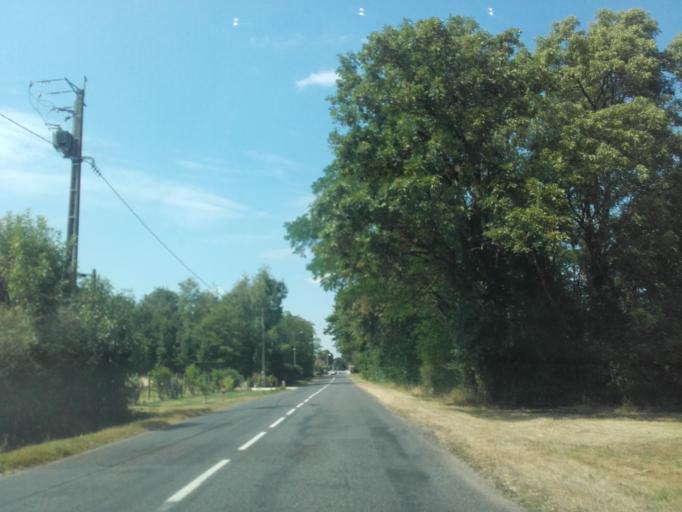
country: FR
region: Rhone-Alpes
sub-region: Departement de l'Ain
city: Villars-les-Dombes
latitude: 46.0591
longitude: 5.0679
